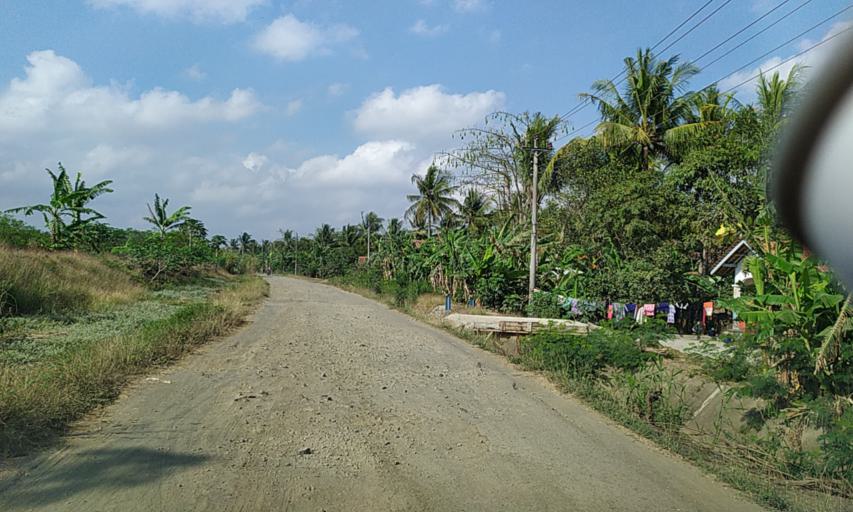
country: ID
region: Central Java
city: Sidakaya
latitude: -7.6089
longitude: 108.8650
